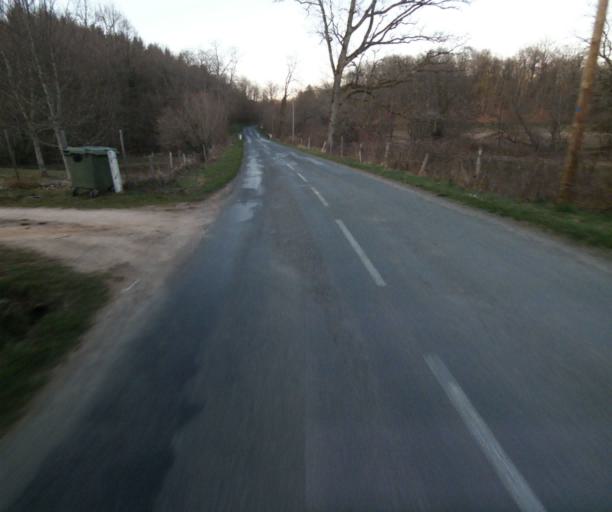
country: FR
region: Limousin
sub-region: Departement de la Correze
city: Saint-Clement
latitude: 45.3438
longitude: 1.6222
